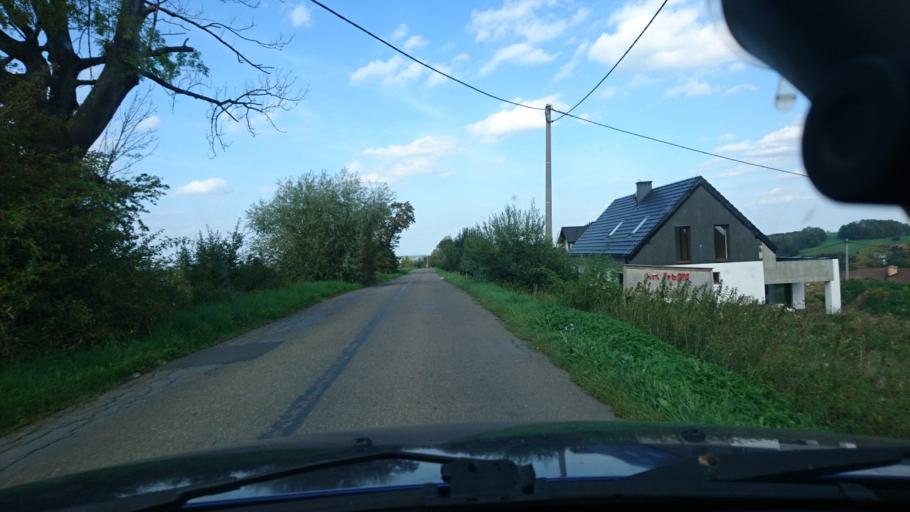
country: PL
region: Silesian Voivodeship
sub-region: Powiat bielski
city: Jasienica
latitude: 49.8285
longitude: 18.9319
